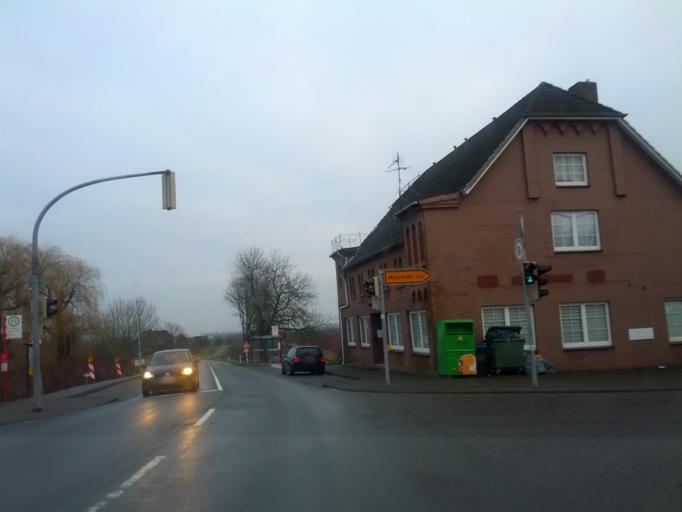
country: DE
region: Lower Saxony
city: Jork
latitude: 53.5190
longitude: 9.7304
